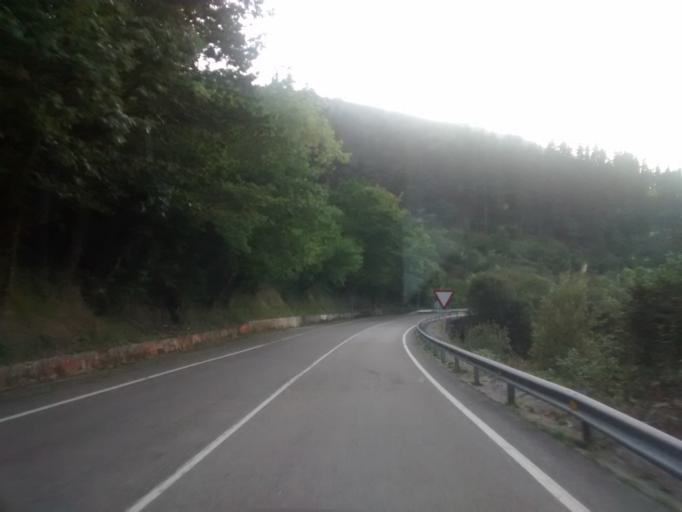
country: ES
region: Cantabria
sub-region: Provincia de Cantabria
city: Ruente
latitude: 43.1693
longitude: -4.2892
